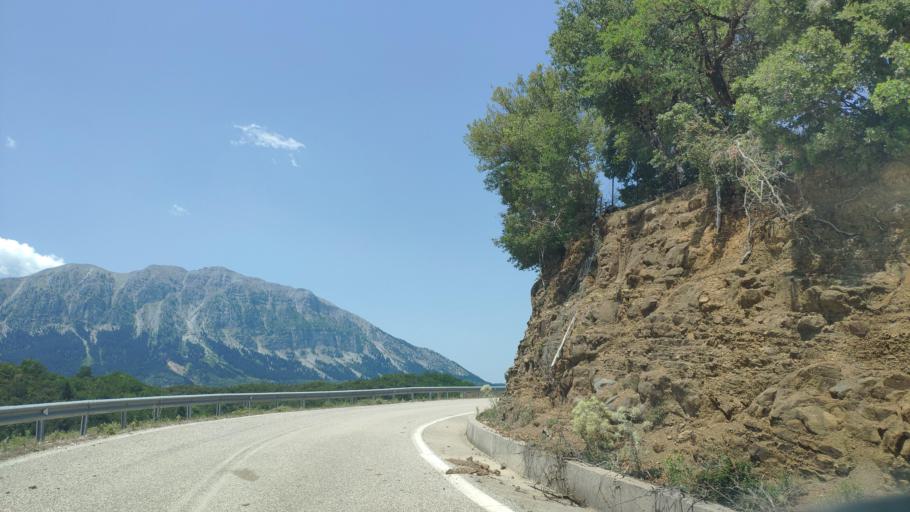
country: GR
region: Epirus
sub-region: Nomos Artas
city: Ano Kalentini
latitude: 39.2204
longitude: 21.3492
